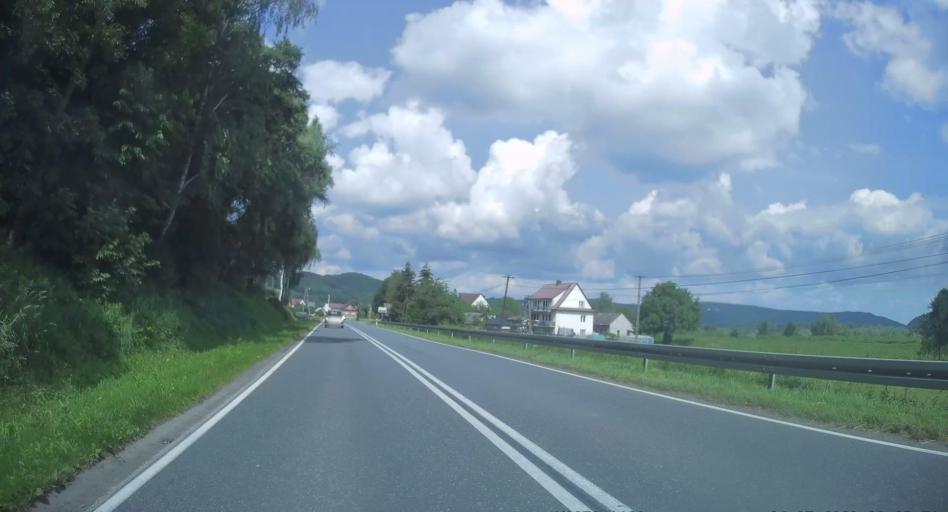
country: PL
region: Lesser Poland Voivodeship
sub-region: Powiat tarnowski
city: Janowice
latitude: 49.8865
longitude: 20.8295
